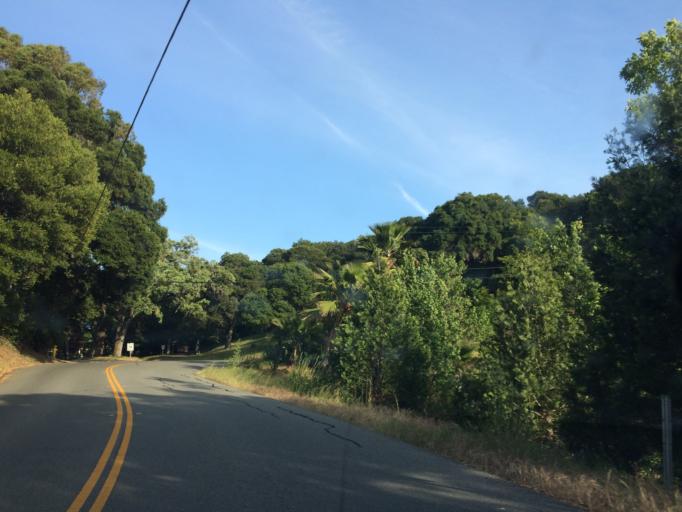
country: US
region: California
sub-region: Santa Clara County
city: Los Altos Hills
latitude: 37.3715
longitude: -122.1688
